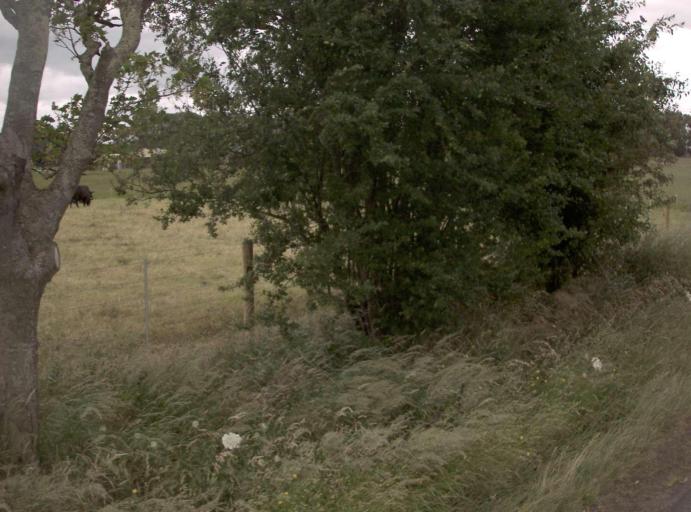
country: AU
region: Victoria
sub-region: Baw Baw
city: Warragul
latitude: -38.1598
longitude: 145.9797
